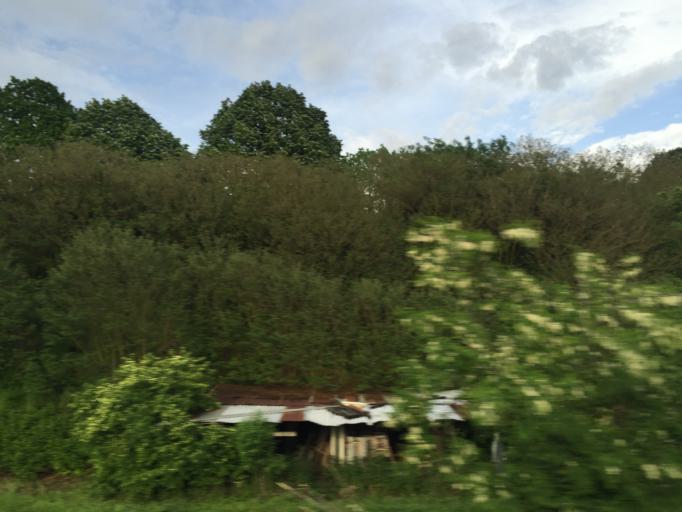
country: FR
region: Rhone-Alpes
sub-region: Departement de l'Ardeche
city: Saint-Jean-de-Muzols
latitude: 45.1167
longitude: 4.8242
